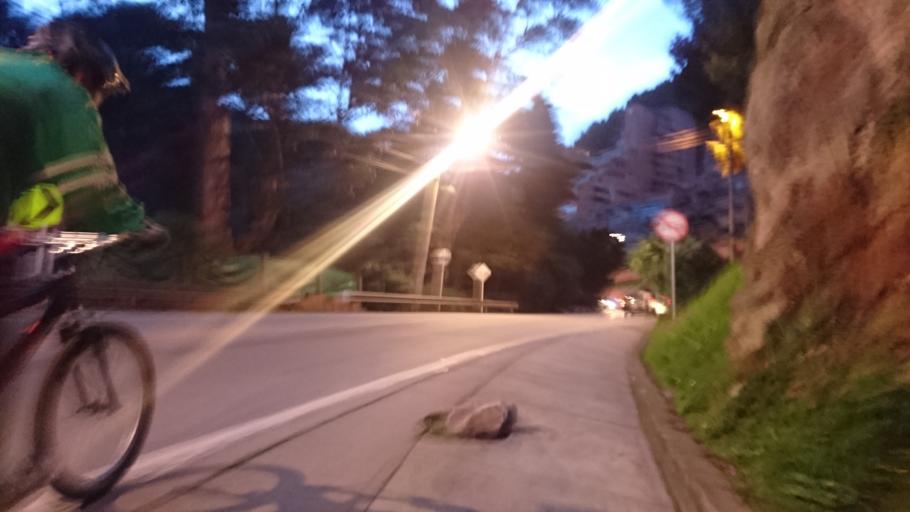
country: CO
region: Bogota D.C.
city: Barrio San Luis
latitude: 4.6701
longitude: -74.0424
